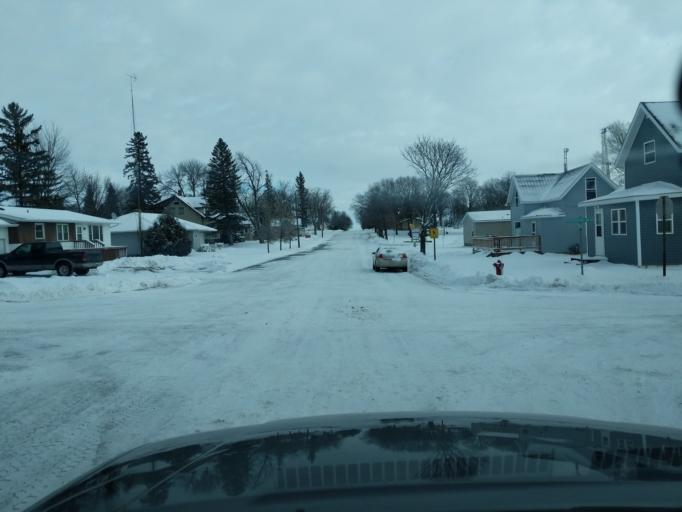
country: US
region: Minnesota
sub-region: Renville County
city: Renville
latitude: 44.7858
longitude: -95.3487
